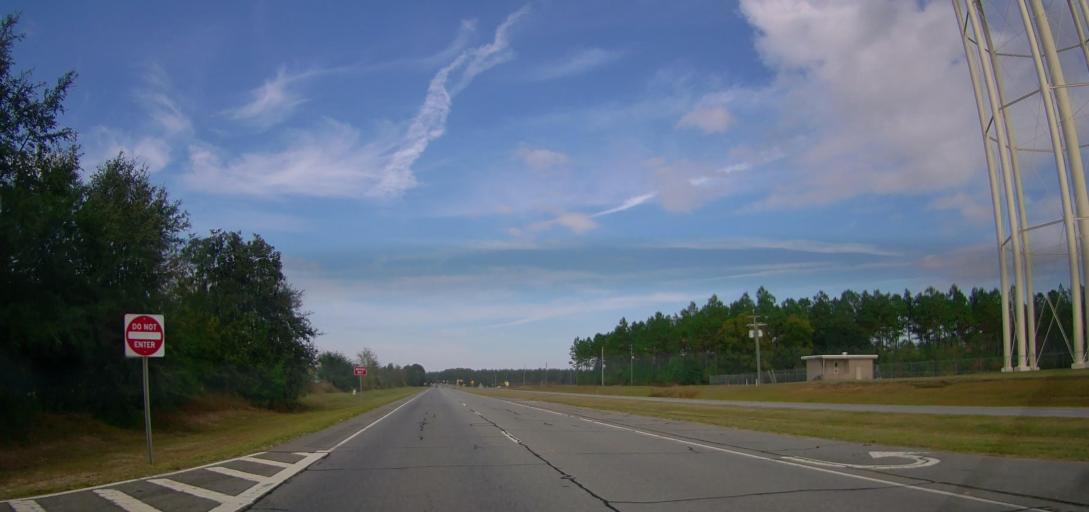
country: US
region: Georgia
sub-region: Mitchell County
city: Camilla
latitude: 31.2743
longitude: -84.1911
